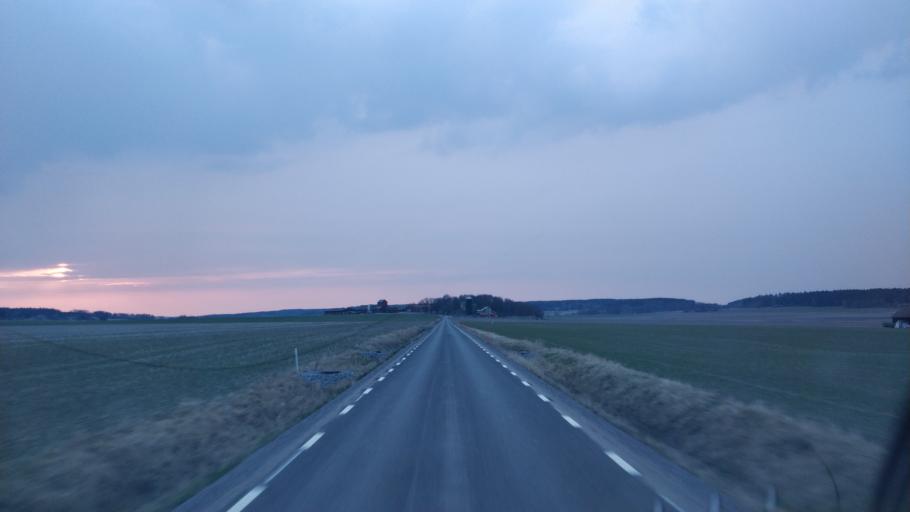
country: SE
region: Uppsala
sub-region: Enkopings Kommun
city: Orsundsbro
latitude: 59.7345
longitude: 17.1937
